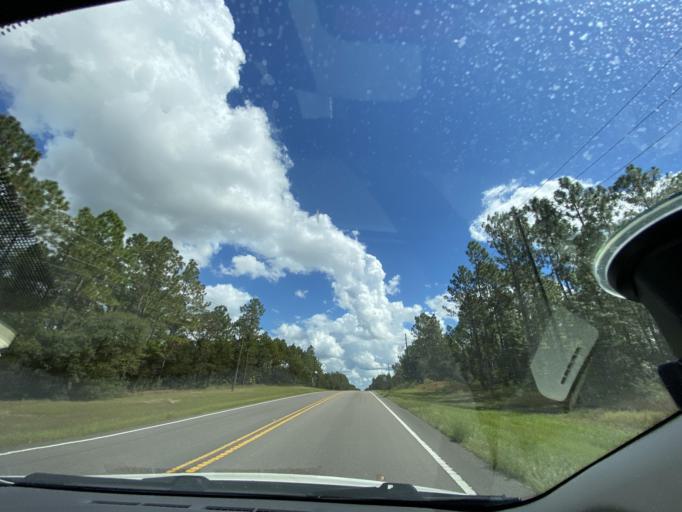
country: US
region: Florida
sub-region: Citrus County
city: Hernando
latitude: 29.0263
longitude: -82.2486
